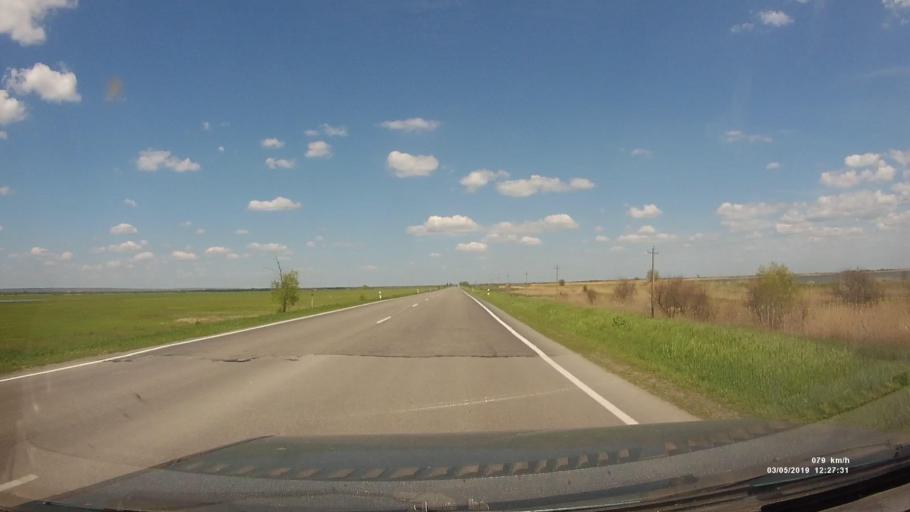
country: RU
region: Rostov
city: Semikarakorsk
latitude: 47.4603
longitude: 40.7215
